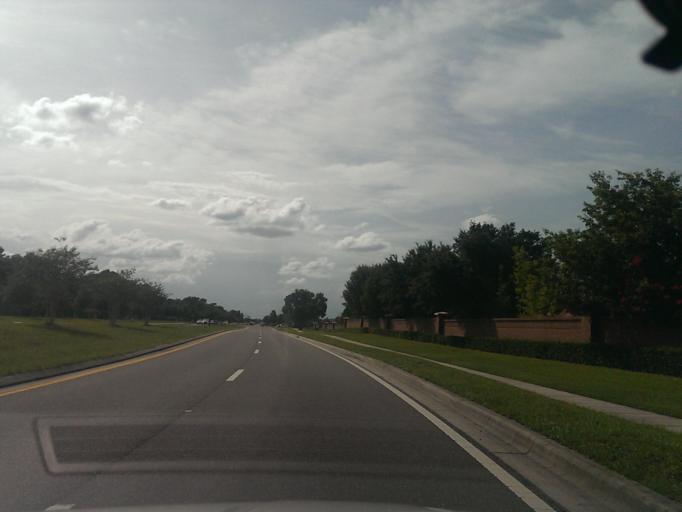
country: US
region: Florida
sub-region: Orange County
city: Windermere
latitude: 28.4692
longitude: -81.5619
